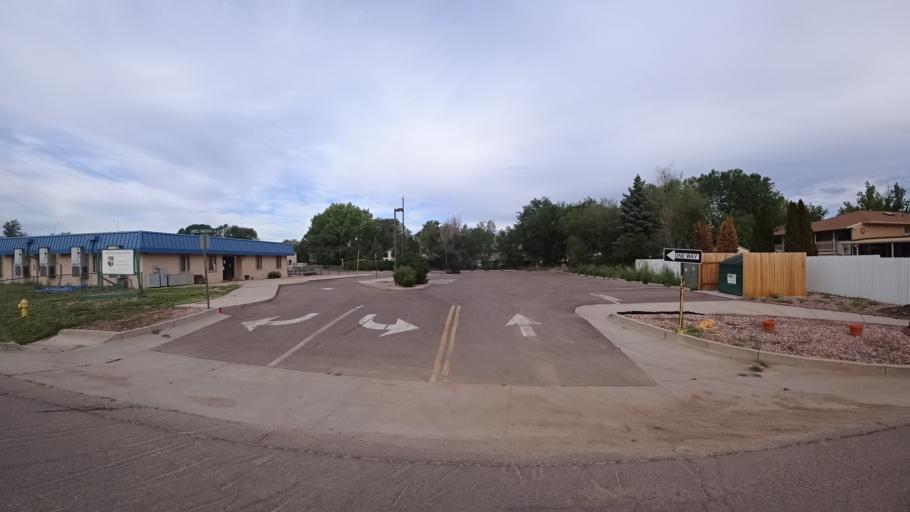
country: US
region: Colorado
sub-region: El Paso County
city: Security-Widefield
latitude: 38.7245
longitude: -104.7152
